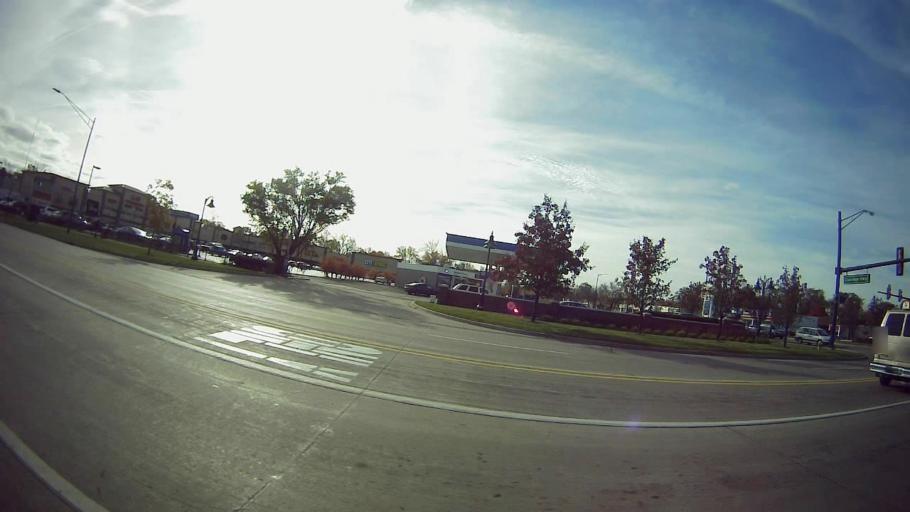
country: US
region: Michigan
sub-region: Oakland County
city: Oak Park
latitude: 42.4599
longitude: -83.1816
